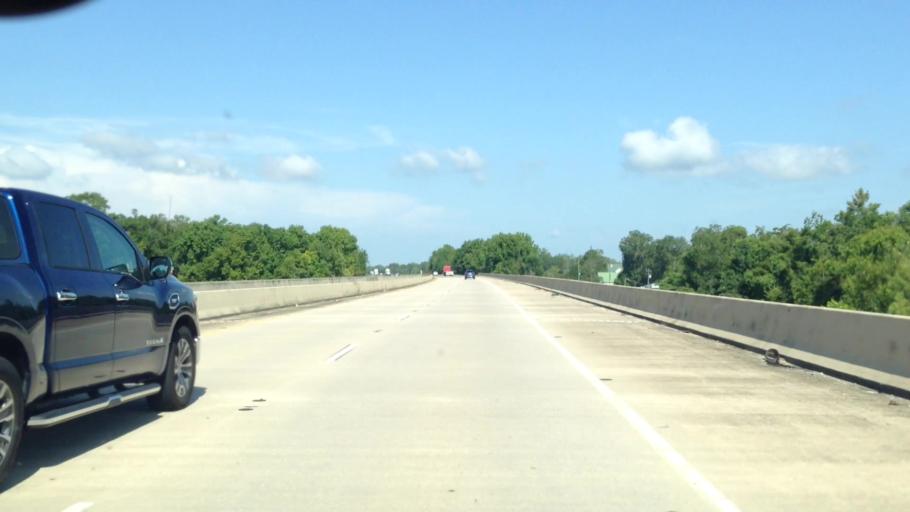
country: US
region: Louisiana
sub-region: Saint Landry Parish
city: Krotz Springs
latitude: 30.5483
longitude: -91.8303
